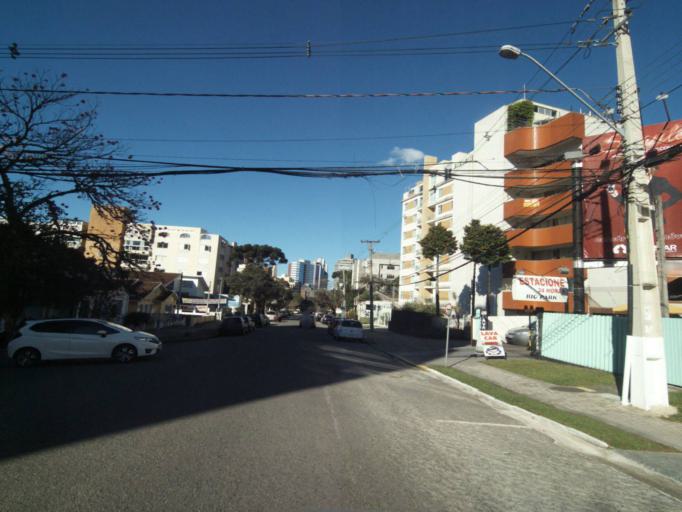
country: BR
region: Parana
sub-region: Curitiba
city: Curitiba
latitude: -25.4110
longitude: -49.2630
